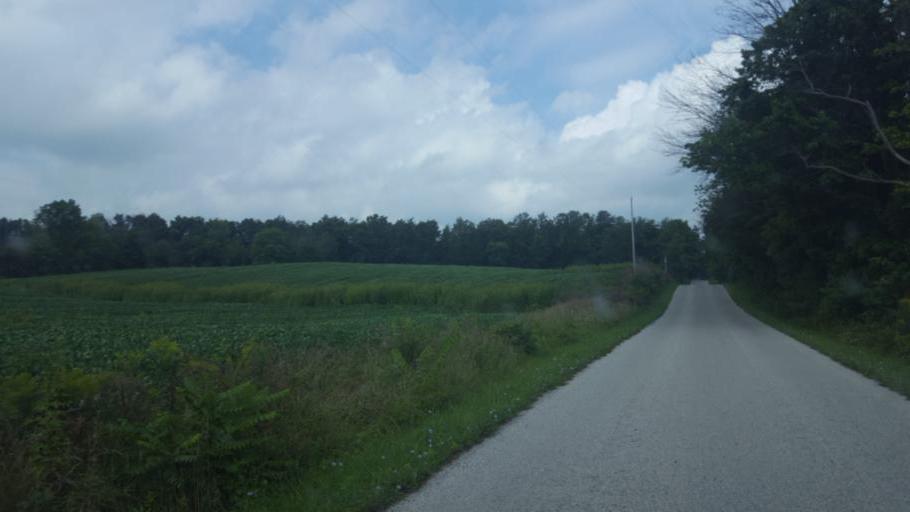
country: US
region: Ohio
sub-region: Morrow County
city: Mount Gilead
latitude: 40.5774
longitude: -82.7002
